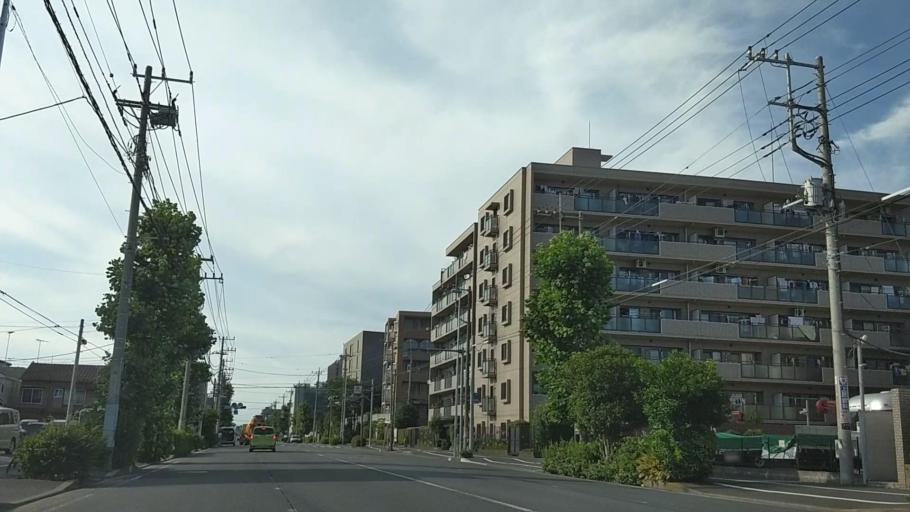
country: JP
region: Kanagawa
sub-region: Kawasaki-shi
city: Kawasaki
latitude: 35.5041
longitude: 139.6938
